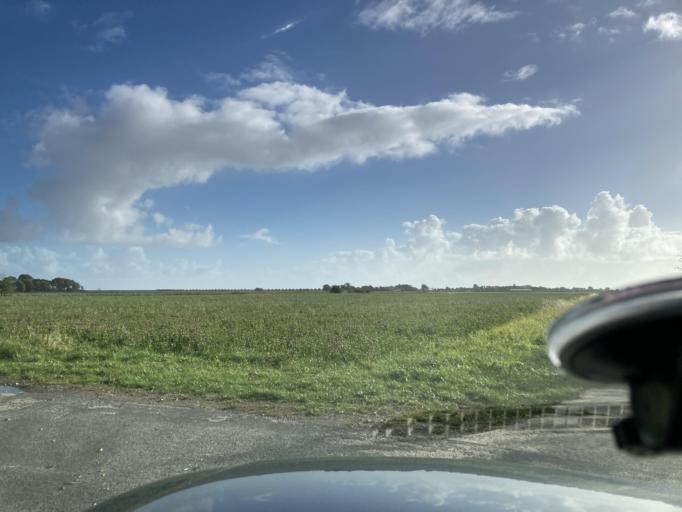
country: DE
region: Schleswig-Holstein
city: Oesterdeichstrich
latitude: 54.1533
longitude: 8.8948
